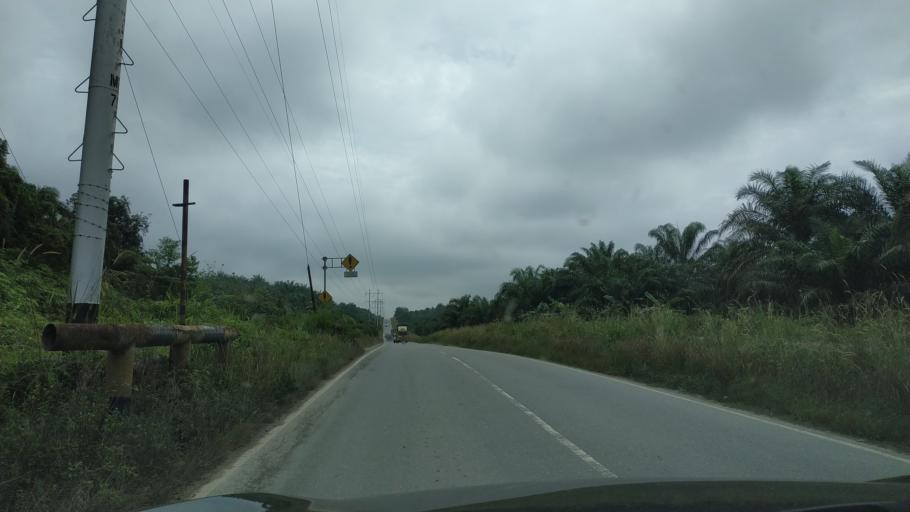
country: ID
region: Riau
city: Pekanbaru
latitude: 0.6435
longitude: 101.6698
